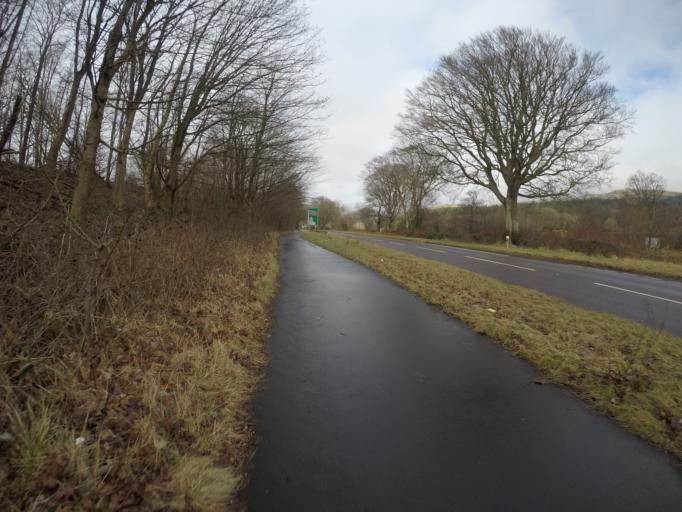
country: GB
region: Scotland
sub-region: North Ayrshire
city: Fairlie
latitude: 55.7350
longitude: -4.8618
